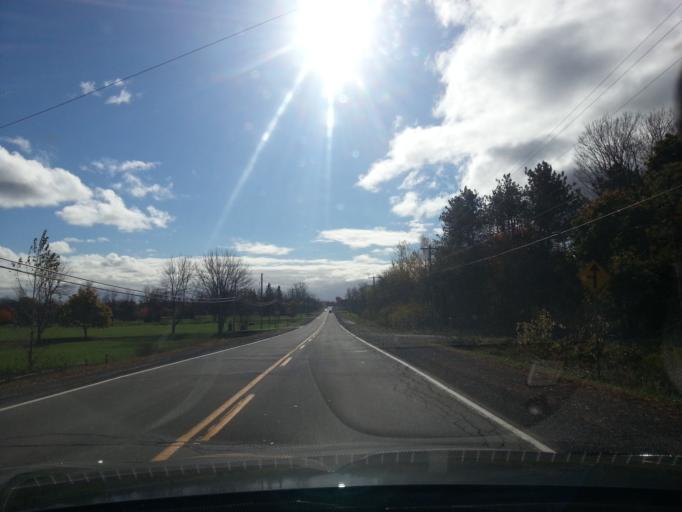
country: CA
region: Ontario
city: Bells Corners
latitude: 45.2041
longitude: -75.6514
